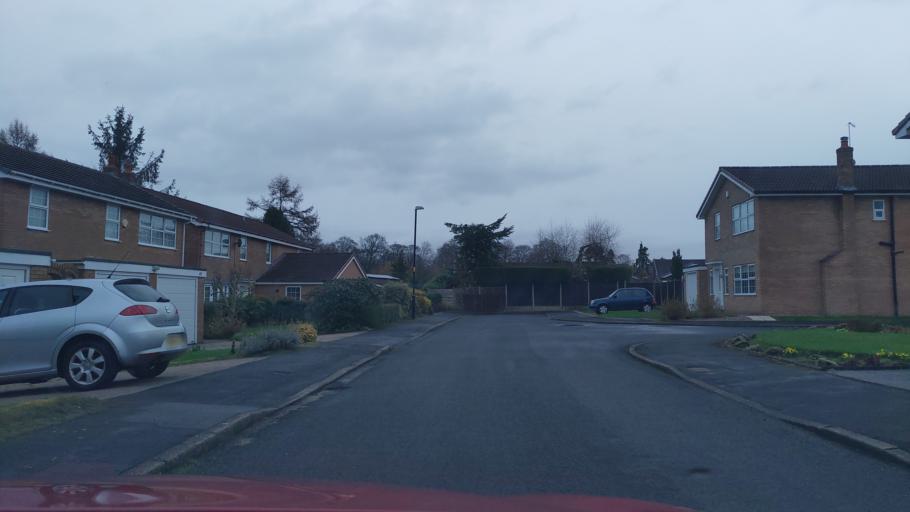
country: GB
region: England
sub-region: Lancashire
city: Euxton
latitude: 53.6634
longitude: -2.6787
